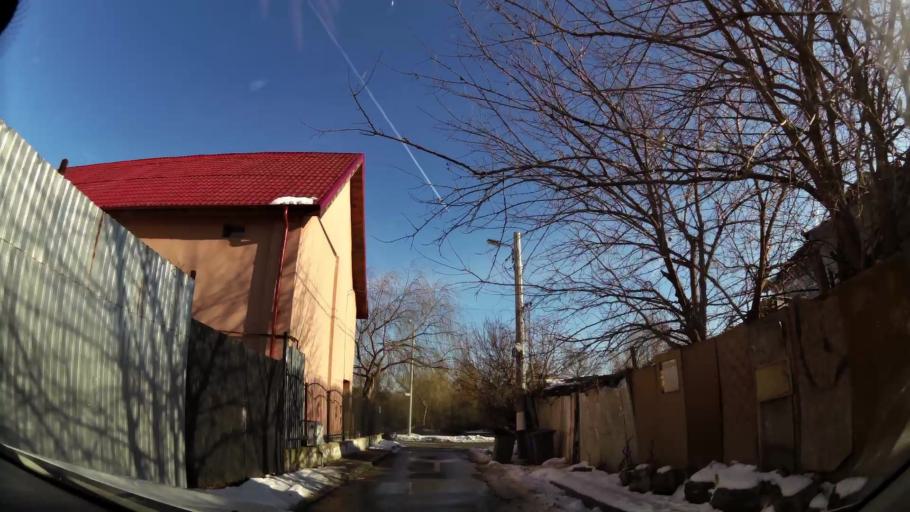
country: RO
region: Ilfov
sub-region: Comuna Fundeni-Dobroesti
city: Fundeni
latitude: 44.4727
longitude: 26.1317
